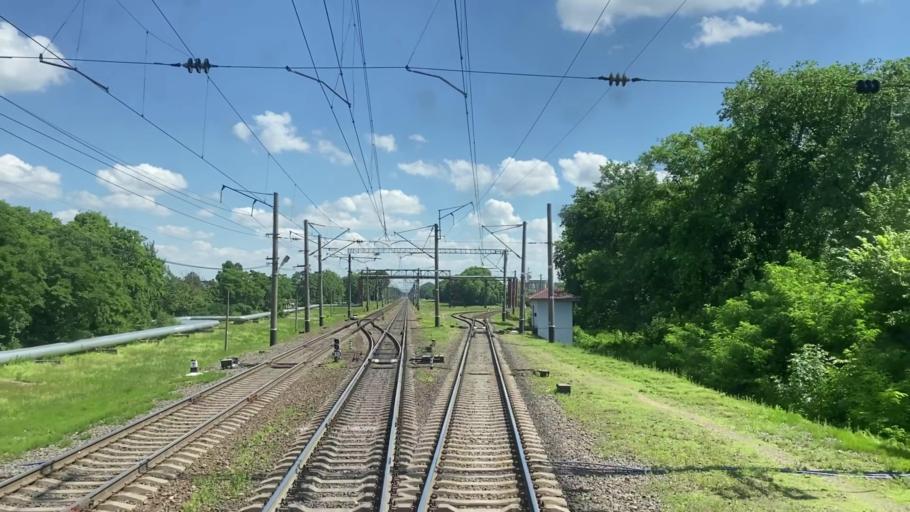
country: BY
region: Brest
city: Baranovichi
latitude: 53.1450
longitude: 26.0257
